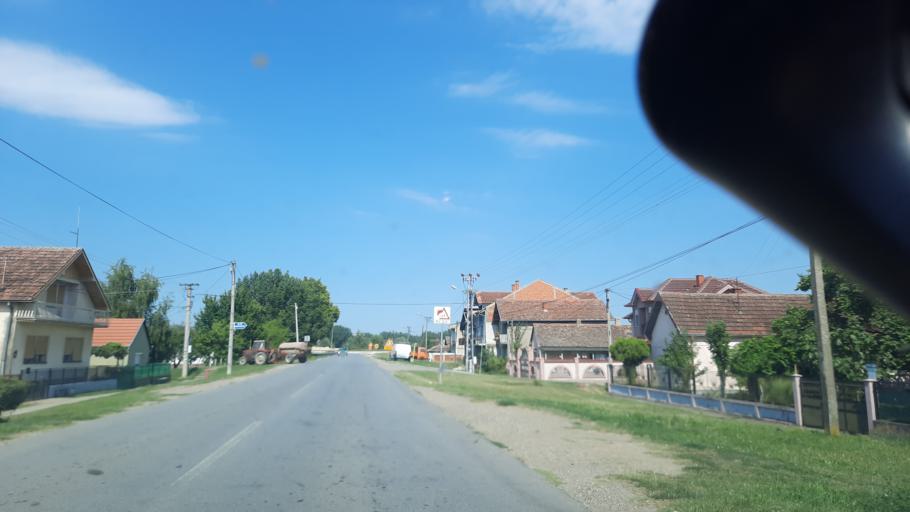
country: RS
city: Macvanska Mitrovica
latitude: 44.9584
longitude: 19.6032
